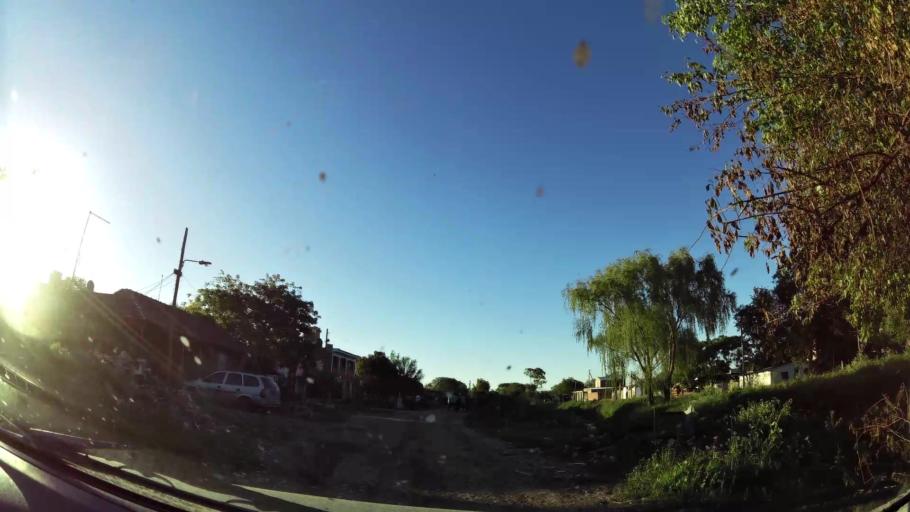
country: AR
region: Buenos Aires
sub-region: Partido de Almirante Brown
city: Adrogue
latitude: -34.7727
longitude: -58.3304
